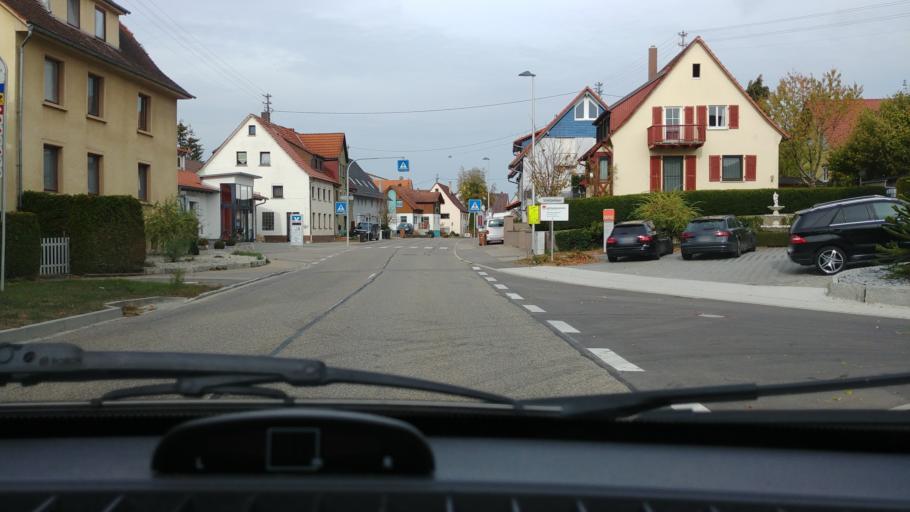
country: DE
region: Baden-Wuerttemberg
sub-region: Regierungsbezirk Stuttgart
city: Stimpfach
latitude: 49.0903
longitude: 10.0634
